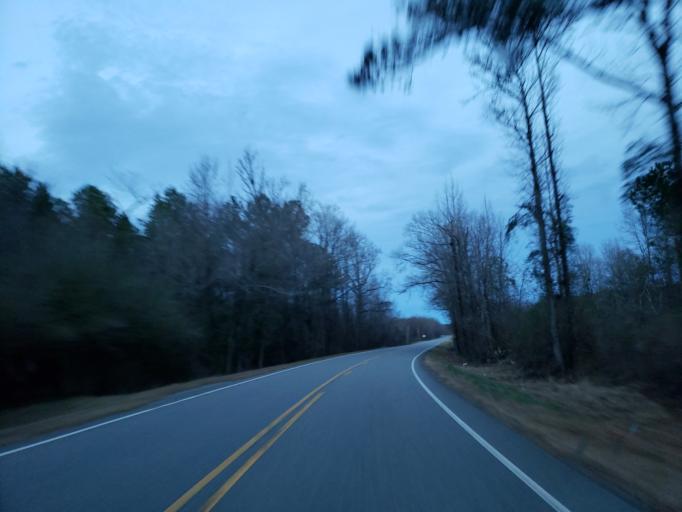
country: US
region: Alabama
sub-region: Greene County
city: Eutaw
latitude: 32.8529
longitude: -88.1103
